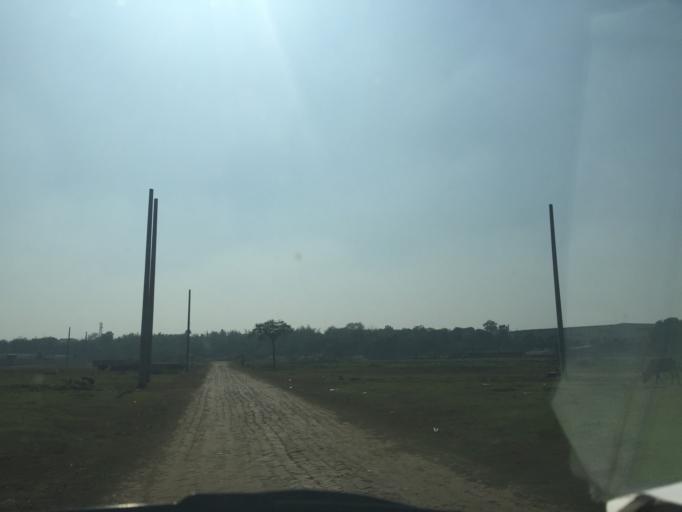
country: BD
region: Dhaka
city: Tungi
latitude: 23.8690
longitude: 90.3135
